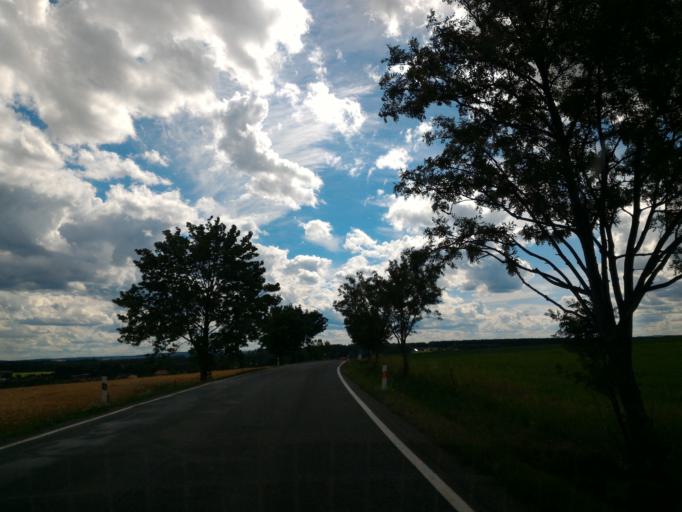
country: CZ
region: Vysocina
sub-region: Okres Jihlava
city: Polna
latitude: 49.4376
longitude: 15.7301
